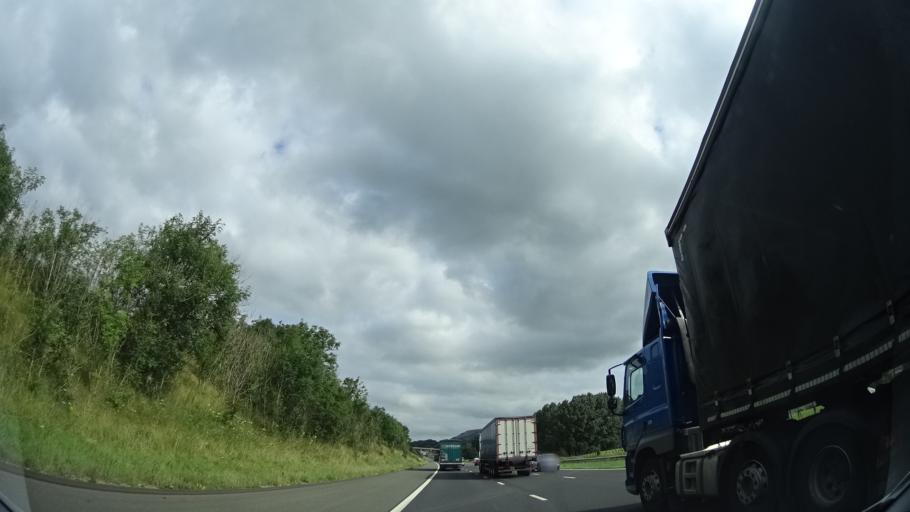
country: GB
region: England
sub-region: Cumbria
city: Milnthorpe
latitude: 54.1873
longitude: -2.7263
